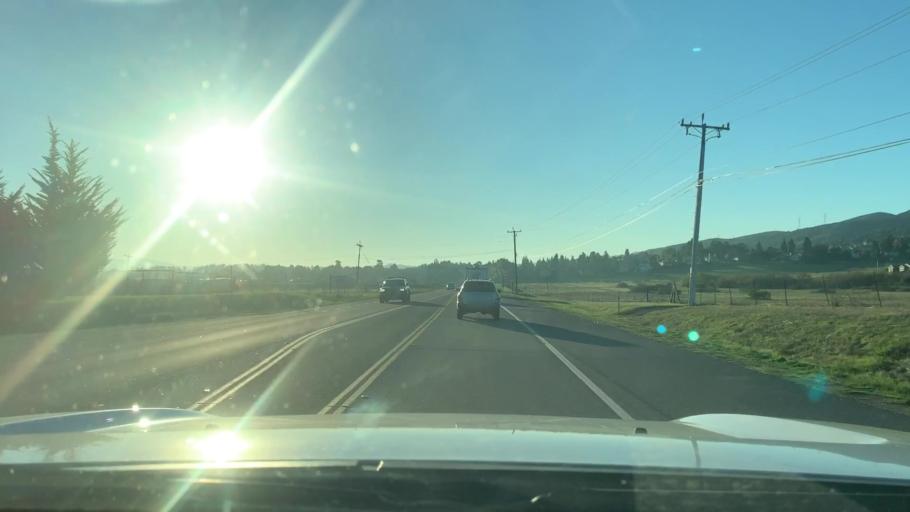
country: US
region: California
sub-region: San Luis Obispo County
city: San Luis Obispo
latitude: 35.2736
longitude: -120.7088
